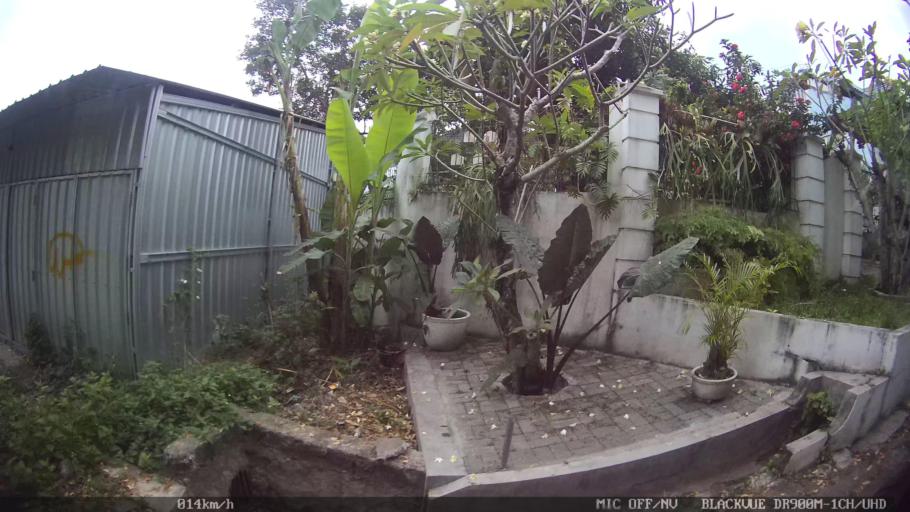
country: ID
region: Daerah Istimewa Yogyakarta
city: Depok
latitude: -7.8112
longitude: 110.4132
